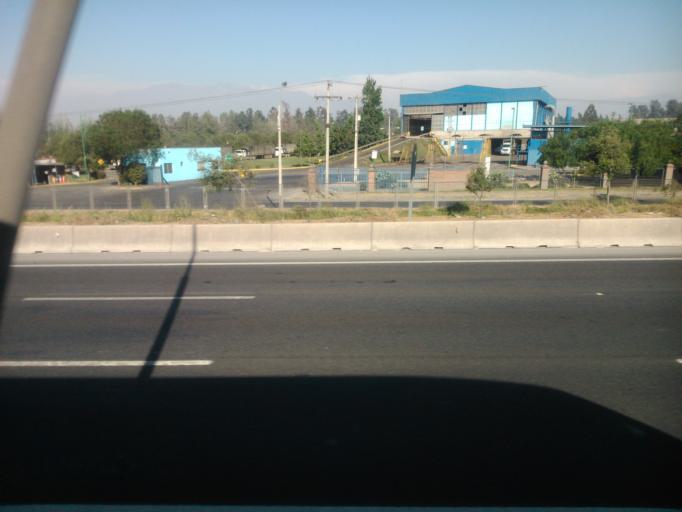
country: CL
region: Santiago Metropolitan
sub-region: Provincia de Maipo
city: San Bernardo
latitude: -33.5393
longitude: -70.7081
